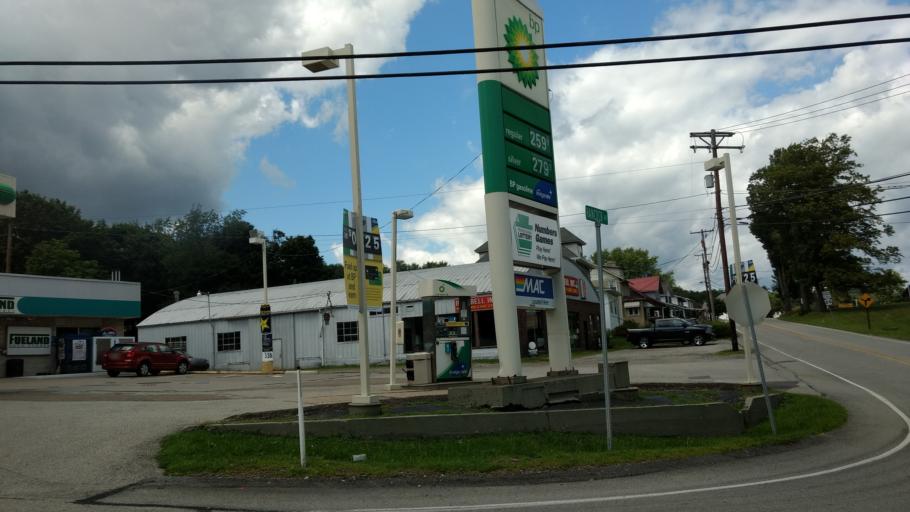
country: US
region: Pennsylvania
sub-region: Armstrong County
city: Apollo
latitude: 40.5706
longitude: -79.5750
